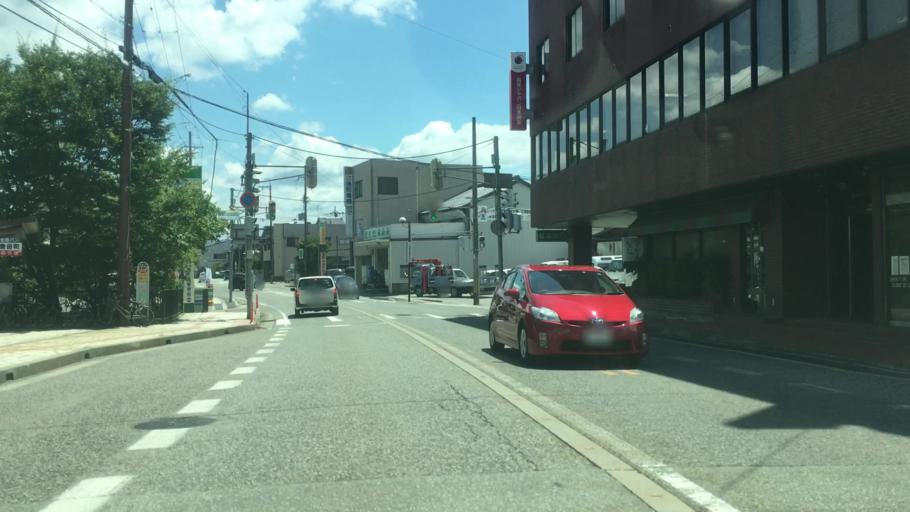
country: JP
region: Hyogo
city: Toyooka
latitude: 35.5405
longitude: 134.8241
